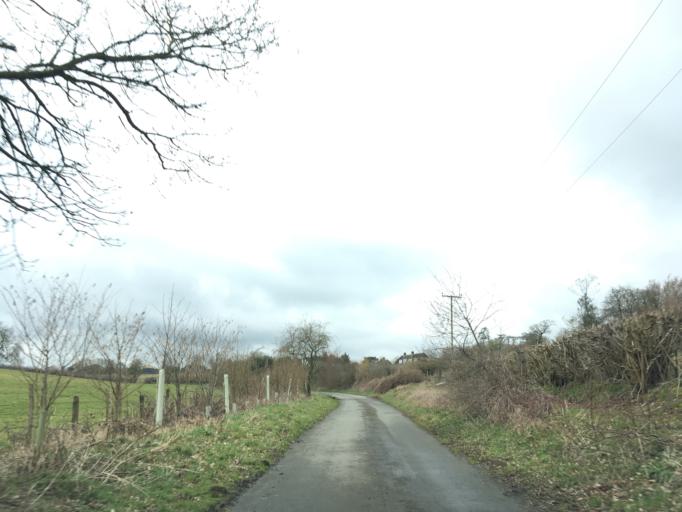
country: GB
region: England
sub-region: West Berkshire
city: Lambourn
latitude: 51.4786
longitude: -1.5392
